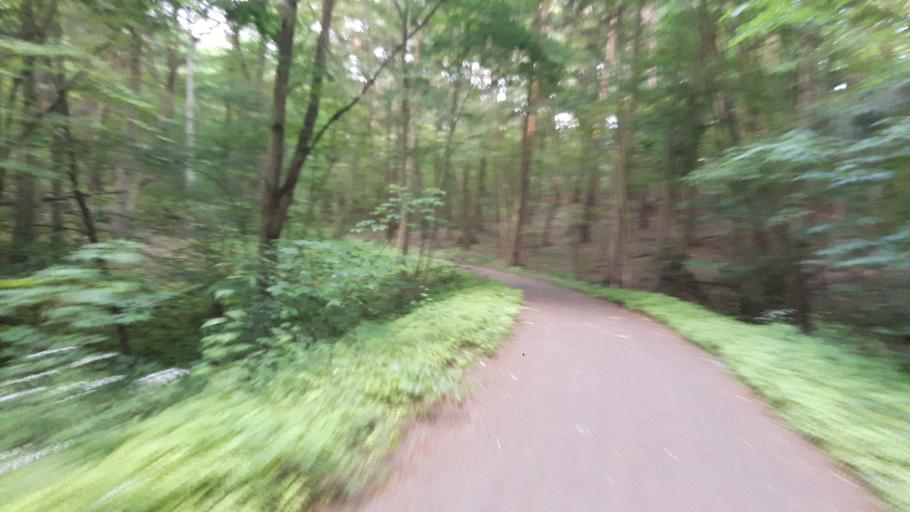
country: DE
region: Brandenburg
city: Mescherin
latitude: 53.2367
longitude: 14.4167
